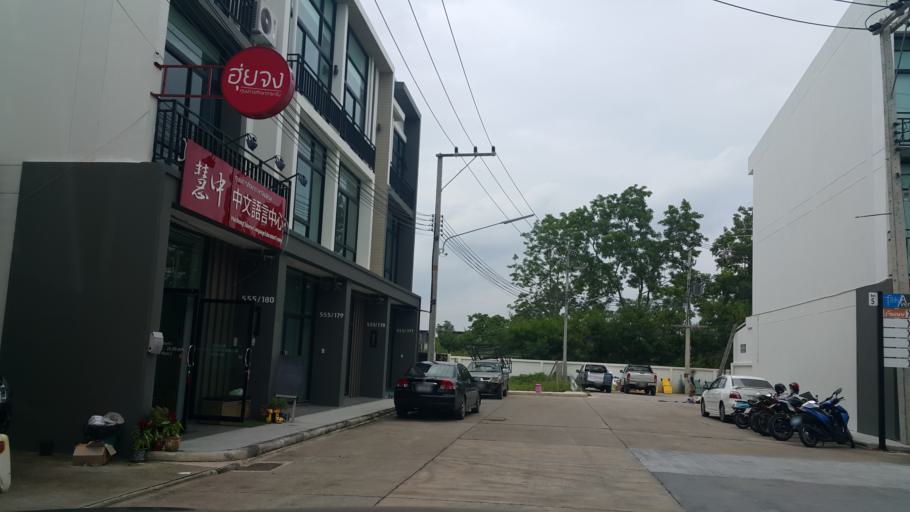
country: TH
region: Chiang Mai
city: San Sai
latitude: 18.8295
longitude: 99.0136
